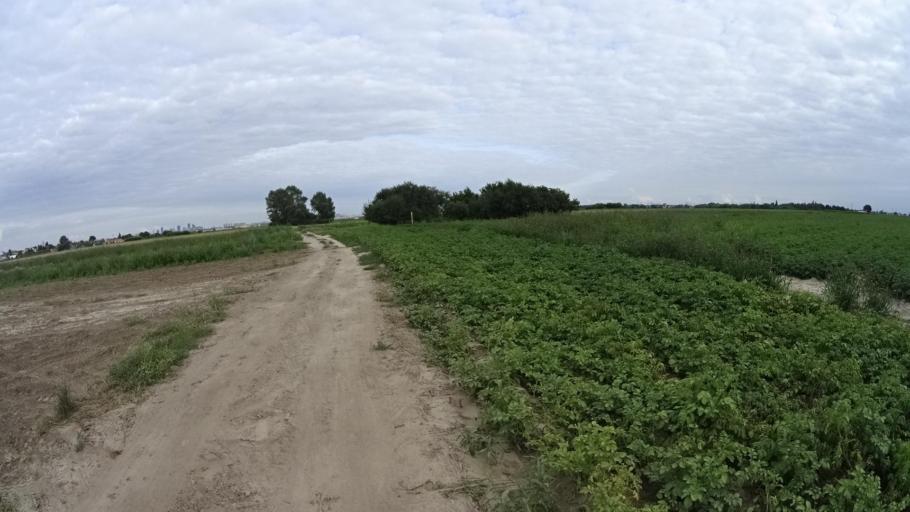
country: PL
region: Masovian Voivodeship
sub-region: Powiat warszawski zachodni
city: Babice
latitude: 52.2406
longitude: 20.8596
